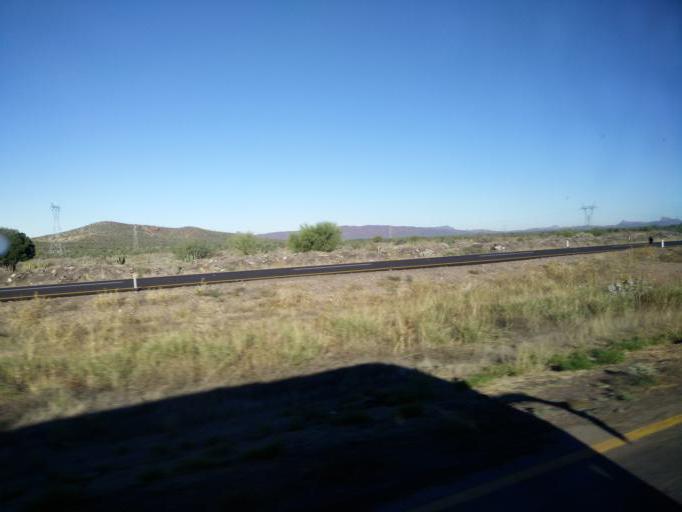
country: MX
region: Sonora
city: Heroica Guaymas
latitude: 28.2947
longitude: -111.0414
